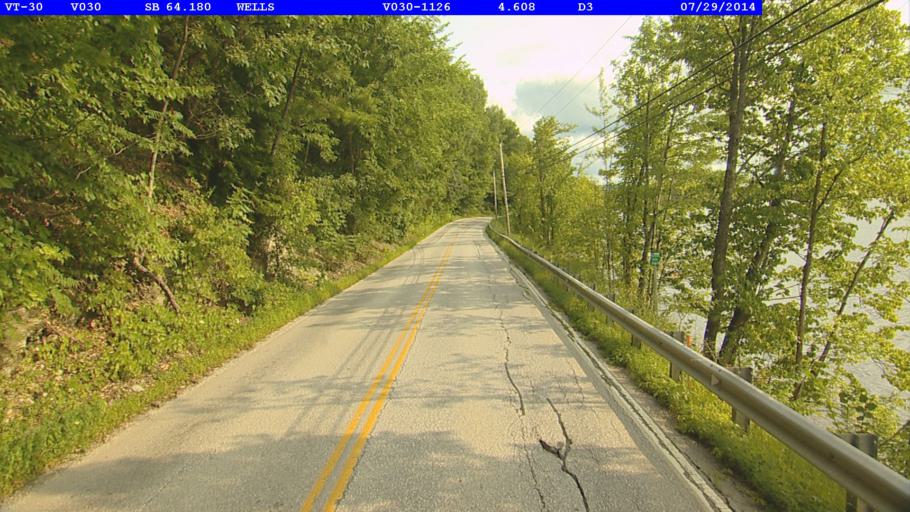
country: US
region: Vermont
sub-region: Rutland County
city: Poultney
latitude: 43.4572
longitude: -73.2052
